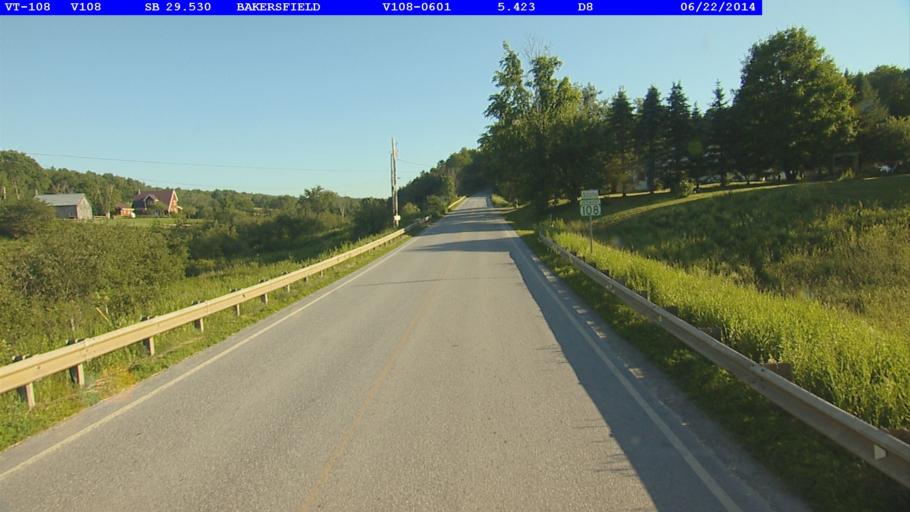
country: US
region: Vermont
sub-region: Franklin County
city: Enosburg Falls
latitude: 44.8049
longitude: -72.7877
